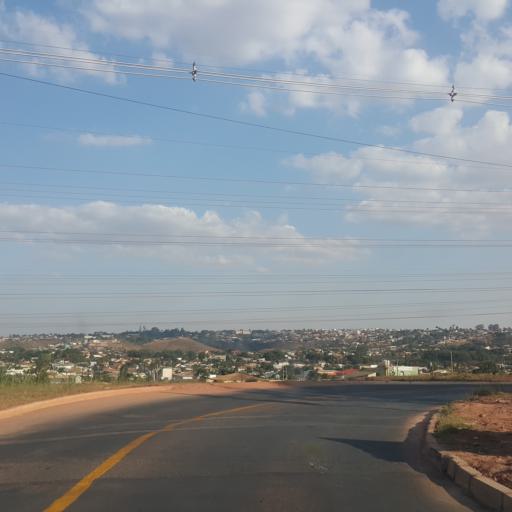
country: BR
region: Federal District
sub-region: Brasilia
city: Brasilia
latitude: -15.8391
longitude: -48.0126
